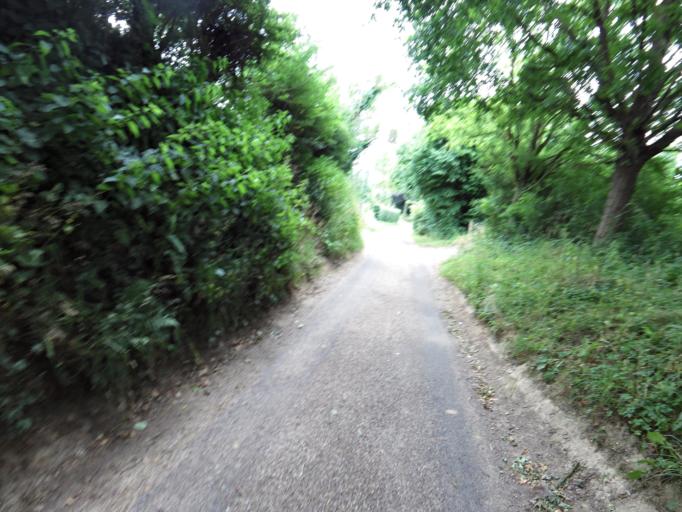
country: NL
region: Limburg
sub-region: Gemeente Simpelveld
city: Simpelveld
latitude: 50.7977
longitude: 5.9405
